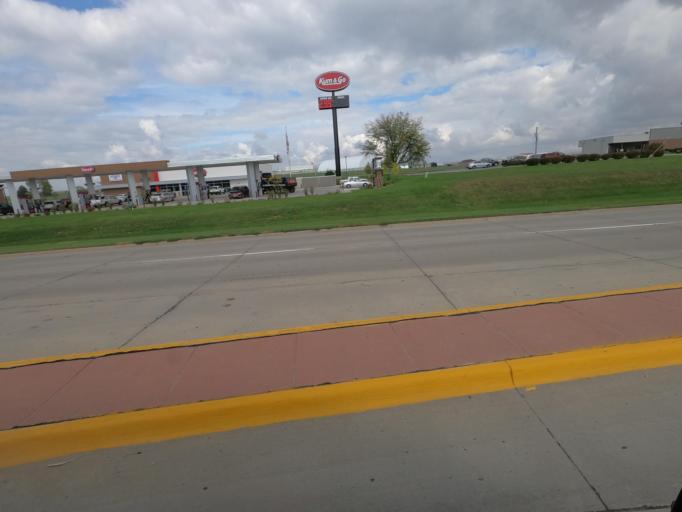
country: US
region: Iowa
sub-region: Story County
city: Ames
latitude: 42.0345
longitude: -93.5753
